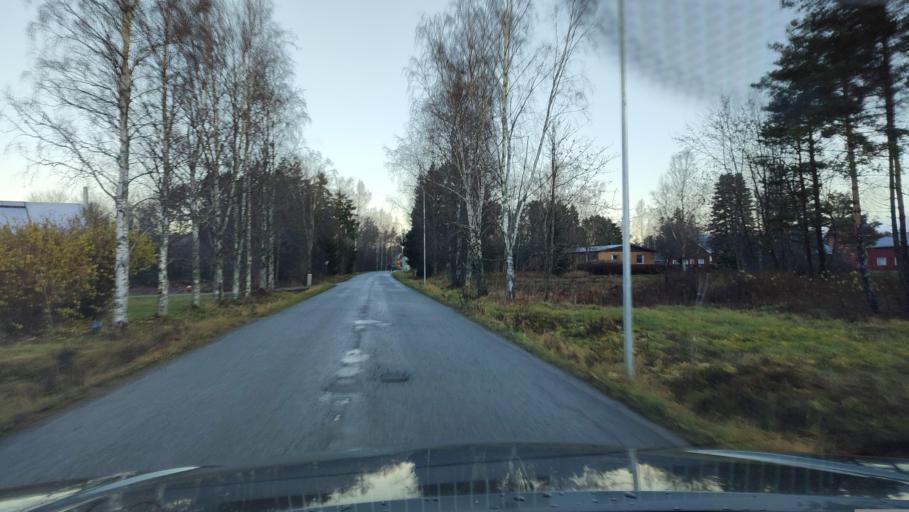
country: FI
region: Ostrobothnia
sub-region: Sydosterbotten
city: Naerpes
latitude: 62.4783
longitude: 21.3580
